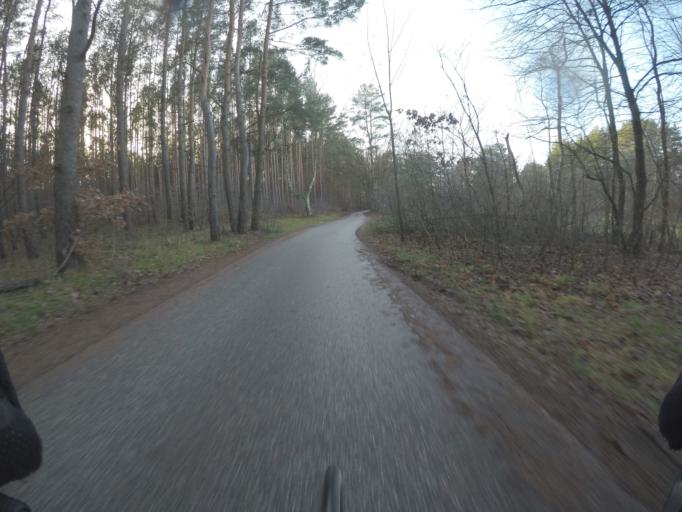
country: DE
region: Brandenburg
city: Hohen Neuendorf
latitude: 52.6842
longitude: 13.2524
